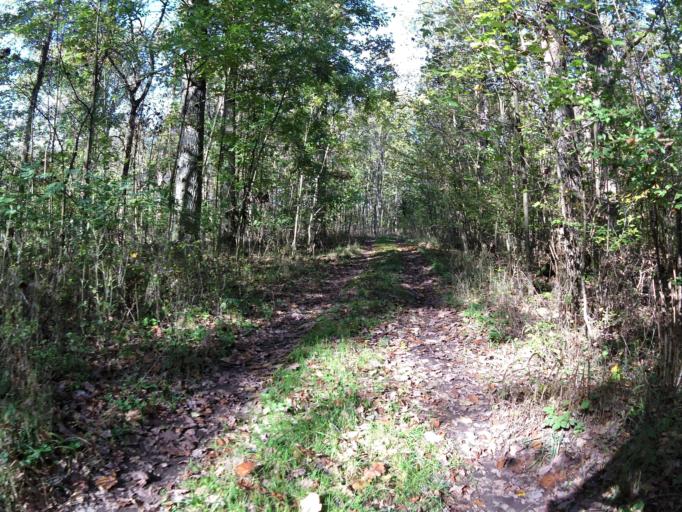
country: DE
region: Bavaria
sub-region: Regierungsbezirk Unterfranken
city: Sulzfeld am Main
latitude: 49.7143
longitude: 10.0985
